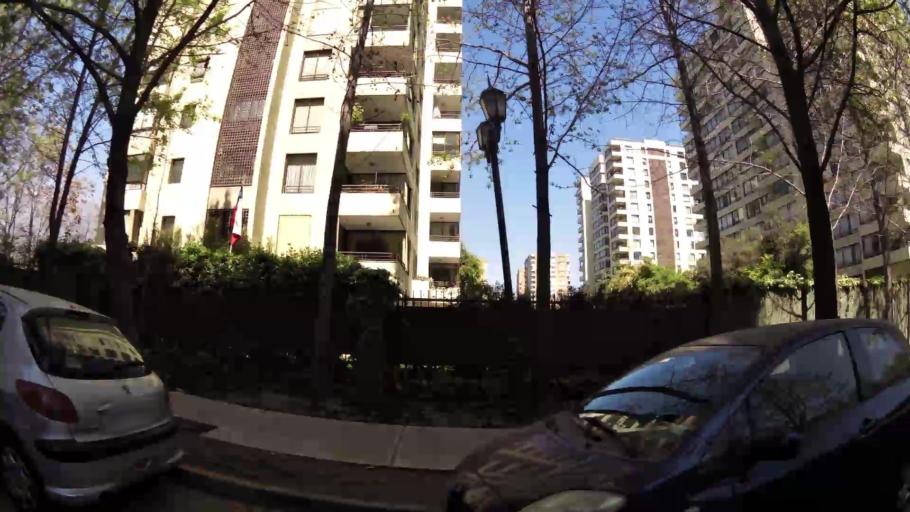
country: CL
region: Santiago Metropolitan
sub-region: Provincia de Santiago
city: Villa Presidente Frei, Nunoa, Santiago, Chile
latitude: -33.4208
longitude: -70.5393
